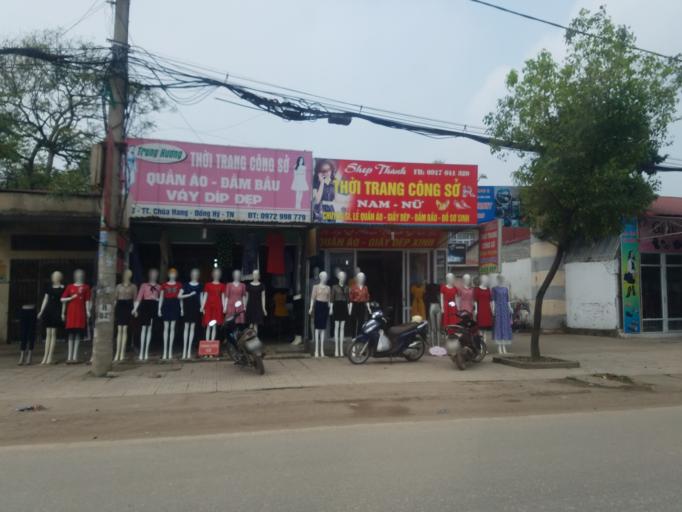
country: VN
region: Thai Nguyen
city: Chua Hang
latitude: 21.6176
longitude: 105.8386
